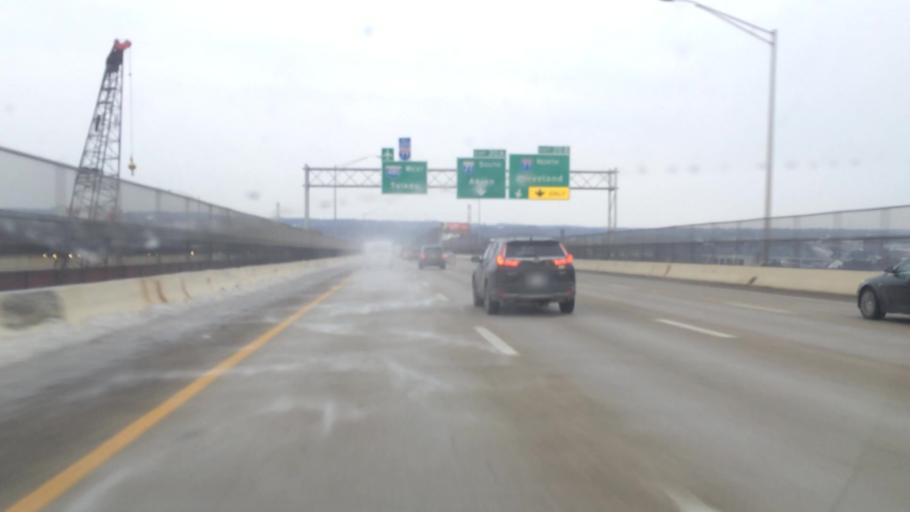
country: US
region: Ohio
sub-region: Cuyahoga County
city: Garfield Heights
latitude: 41.4101
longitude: -81.6259
